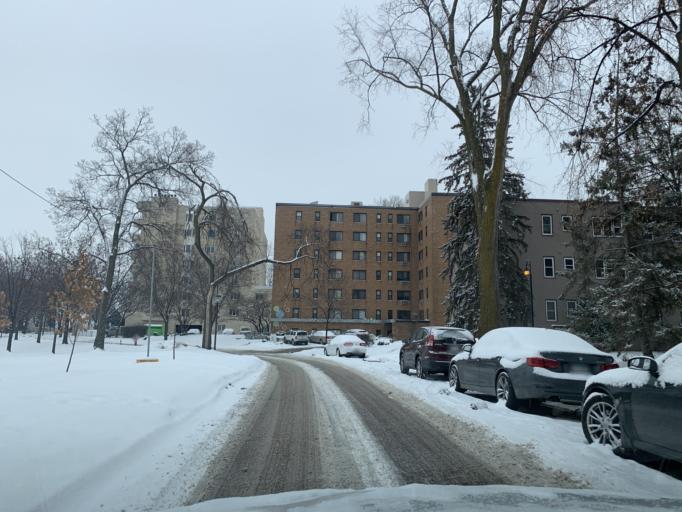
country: US
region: Minnesota
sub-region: Hennepin County
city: Saint Louis Park
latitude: 44.9463
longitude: -93.3209
